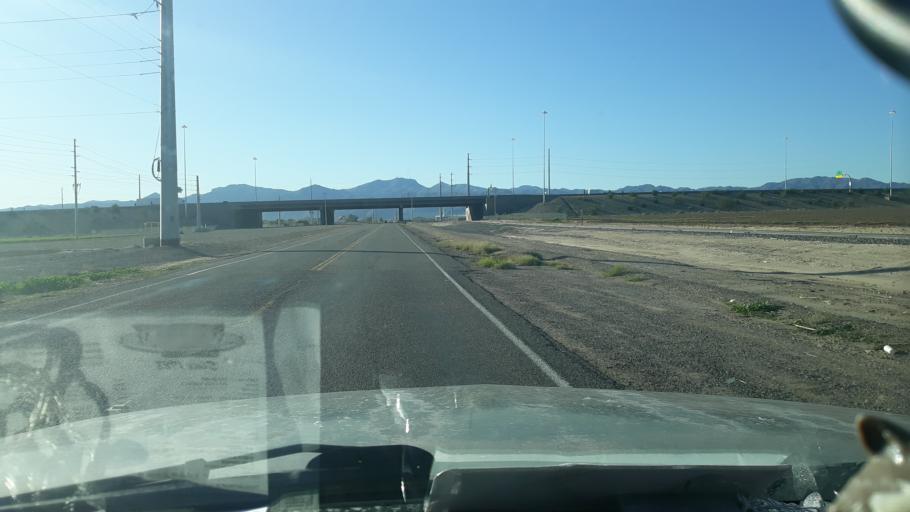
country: US
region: Arizona
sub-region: Maricopa County
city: Citrus Park
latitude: 33.5665
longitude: -112.4141
